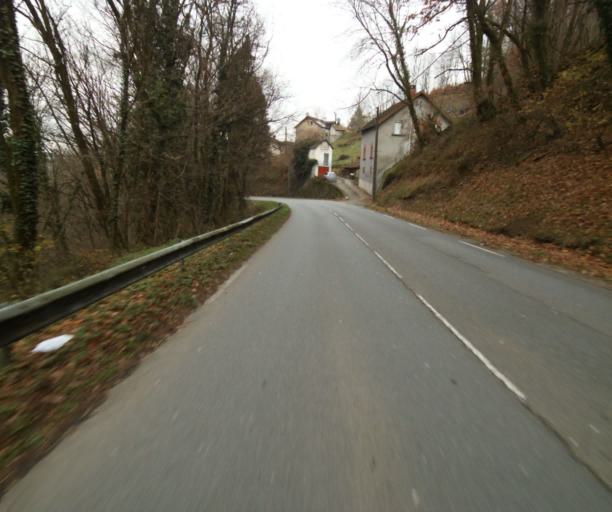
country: FR
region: Limousin
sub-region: Departement de la Correze
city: Tulle
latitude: 45.2658
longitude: 1.7433
